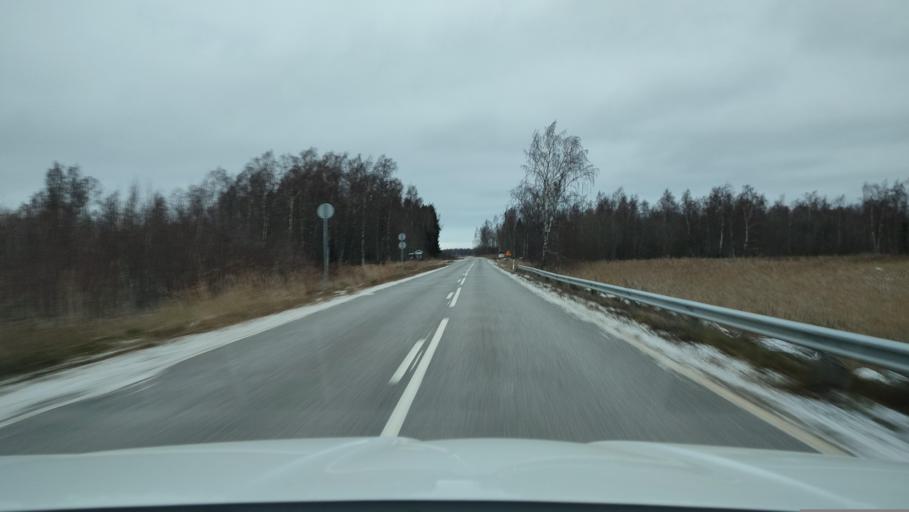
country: FI
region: Ostrobothnia
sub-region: Vaasa
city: Replot
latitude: 63.2778
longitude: 21.3419
